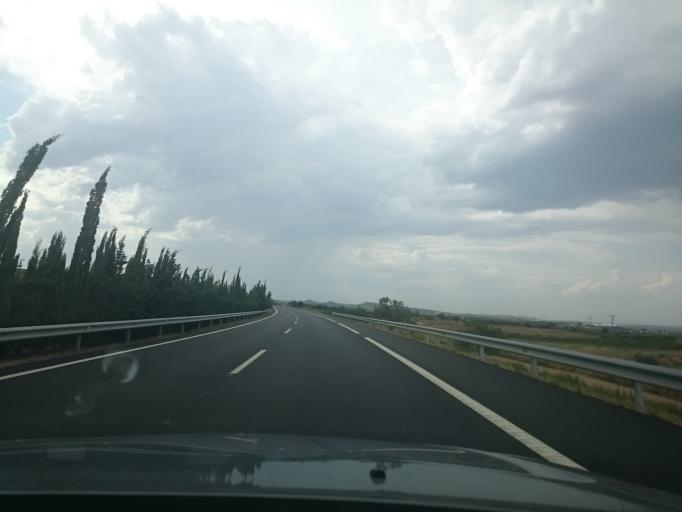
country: ES
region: La Rioja
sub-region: Provincia de La Rioja
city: Aldeanueva de Ebro
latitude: 42.2489
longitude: -1.9066
